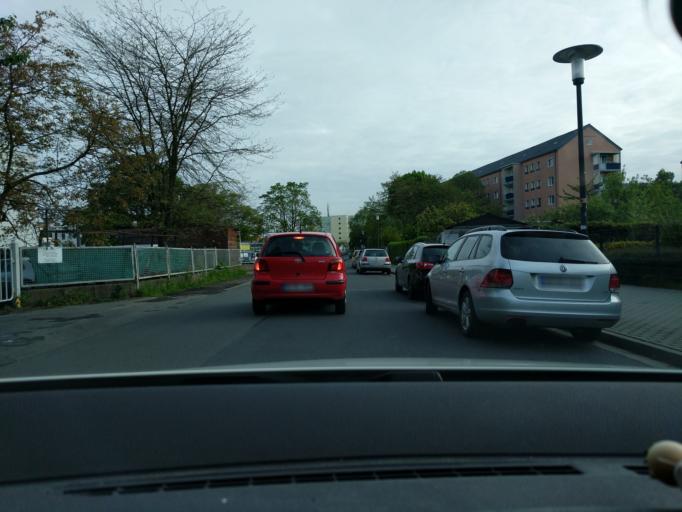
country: DE
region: Saxony
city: Albertstadt
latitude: 51.0420
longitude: 13.7827
